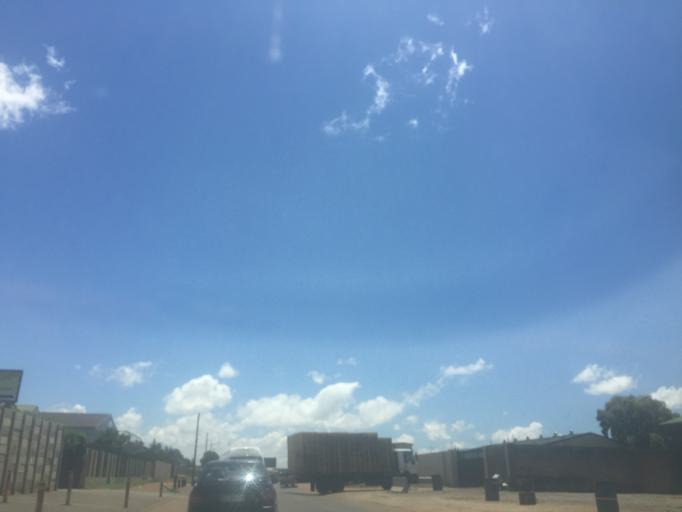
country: ZA
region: Mpumalanga
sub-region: Nkangala District Municipality
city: Delmas
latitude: -26.1327
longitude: 28.6891
